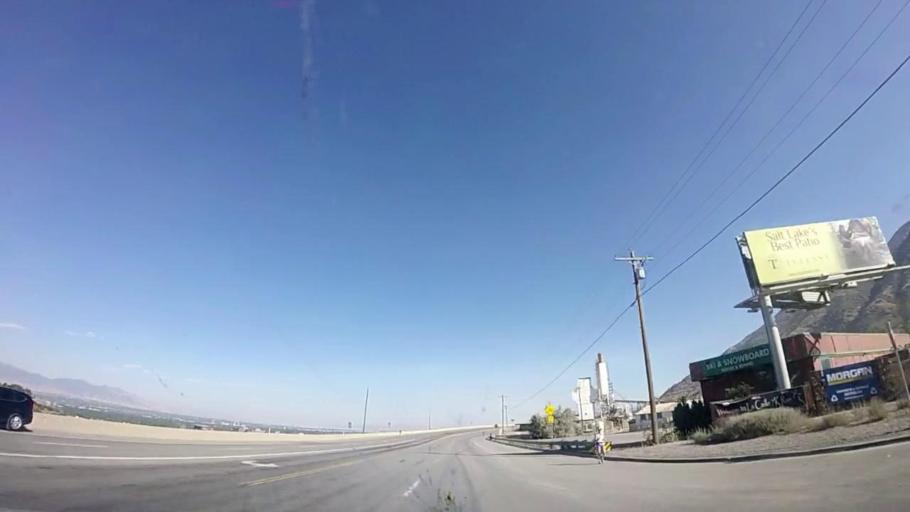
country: US
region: Utah
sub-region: Salt Lake County
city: Cottonwood Heights
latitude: 40.6278
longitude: -111.7987
